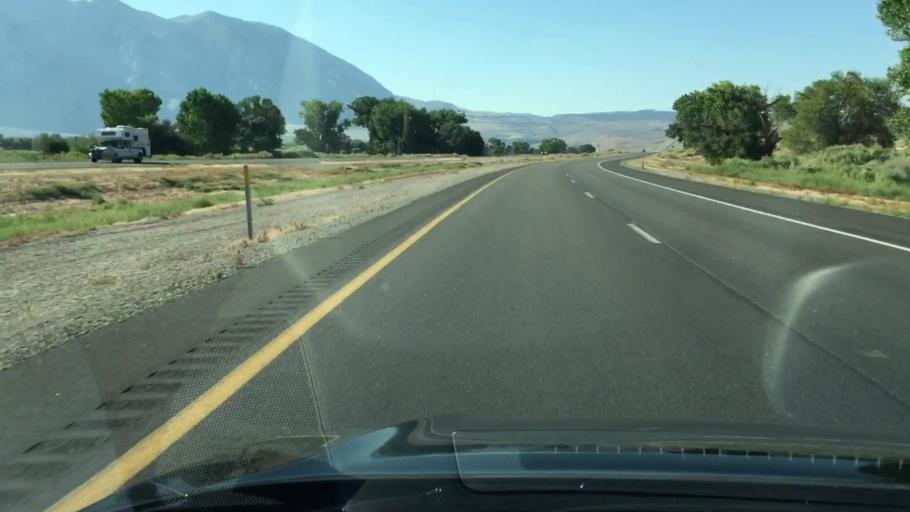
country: US
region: California
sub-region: Inyo County
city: West Bishop
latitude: 37.4112
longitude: -118.5507
